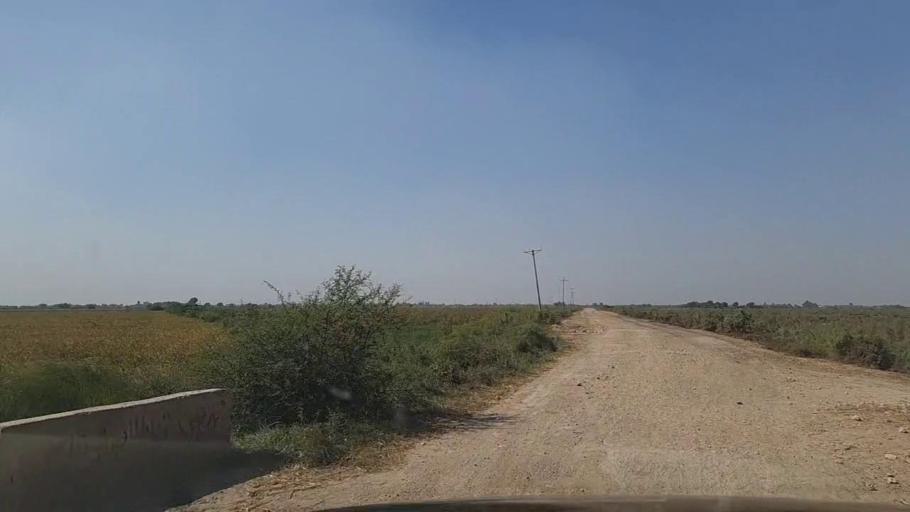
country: PK
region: Sindh
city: Daro Mehar
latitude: 24.8340
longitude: 68.1703
